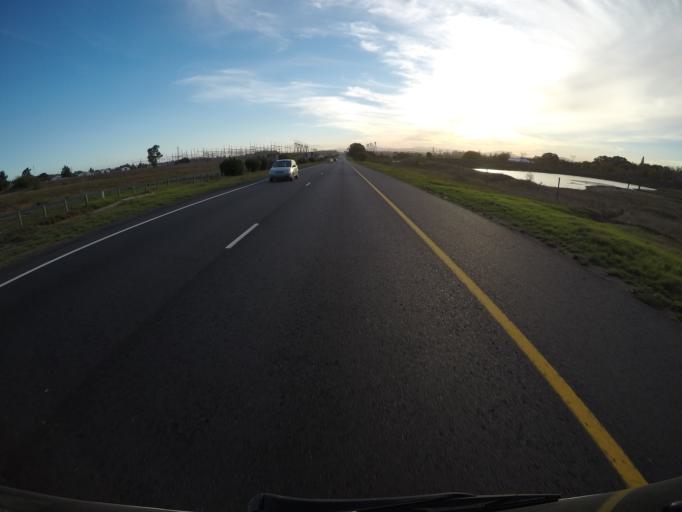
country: ZA
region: Western Cape
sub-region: City of Cape Town
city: Kraaifontein
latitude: -33.8139
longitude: 18.8126
